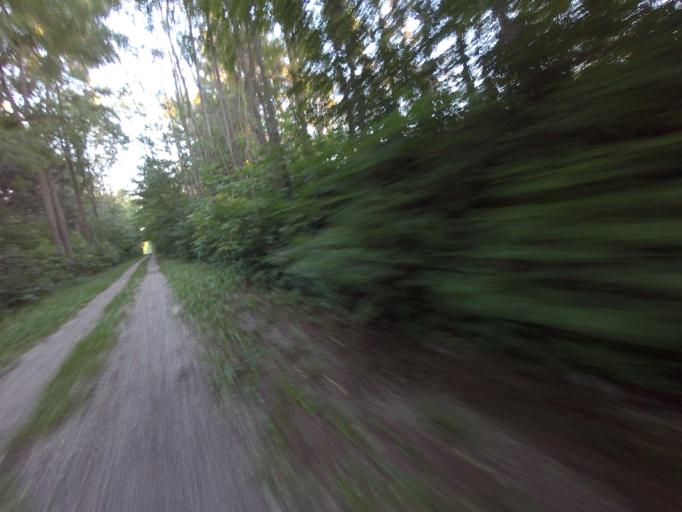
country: CA
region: Ontario
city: Goderich
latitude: 43.7505
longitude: -81.6585
